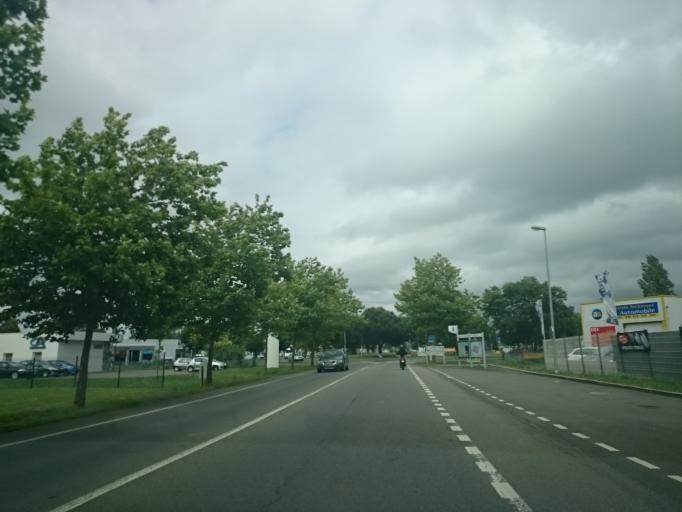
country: FR
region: Pays de la Loire
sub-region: Departement de la Loire-Atlantique
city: La Montagne
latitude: 47.1759
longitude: -1.6807
